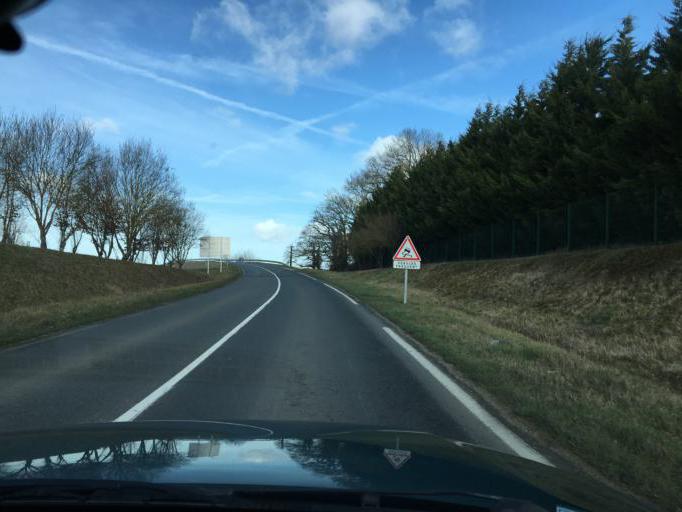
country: FR
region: Centre
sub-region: Departement du Loiret
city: Saint-Ay
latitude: 47.8483
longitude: 1.7249
